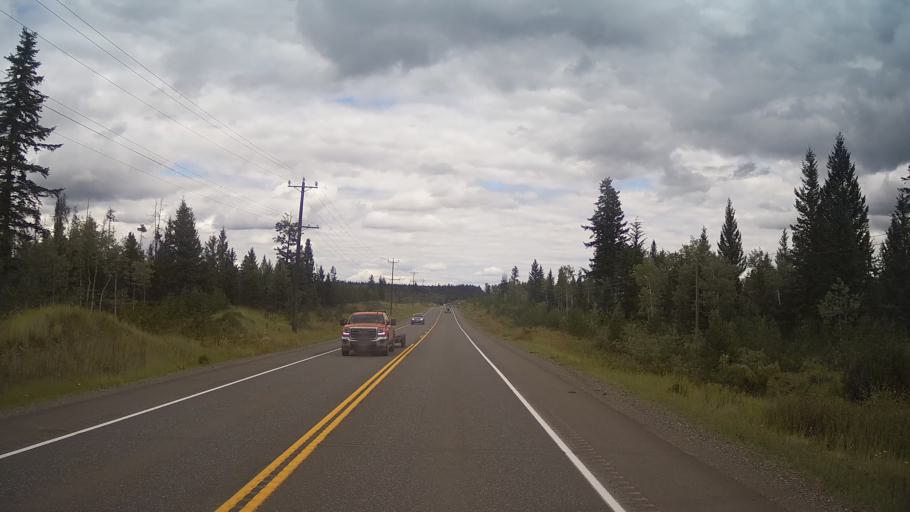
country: CA
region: British Columbia
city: Cache Creek
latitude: 51.2505
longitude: -121.4779
